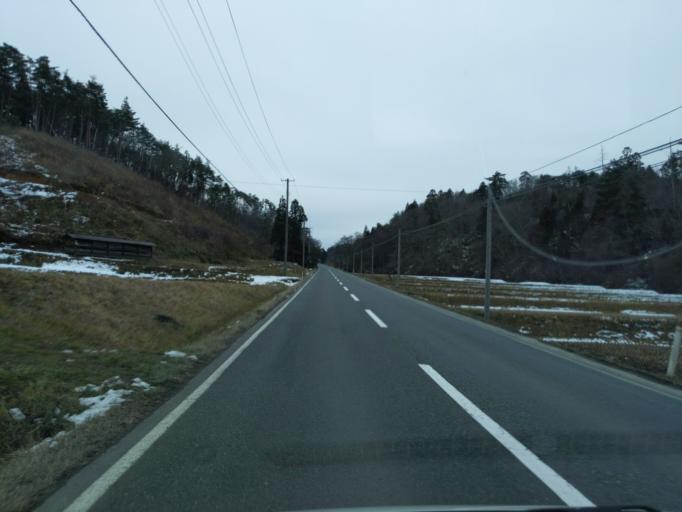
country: JP
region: Iwate
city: Mizusawa
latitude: 39.1486
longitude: 141.2431
